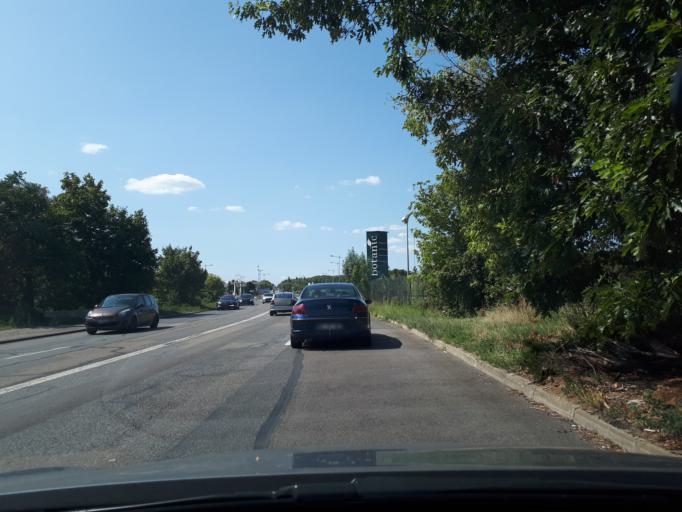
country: FR
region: Rhone-Alpes
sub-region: Departement du Rhone
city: Bron
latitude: 45.7237
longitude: 4.9381
